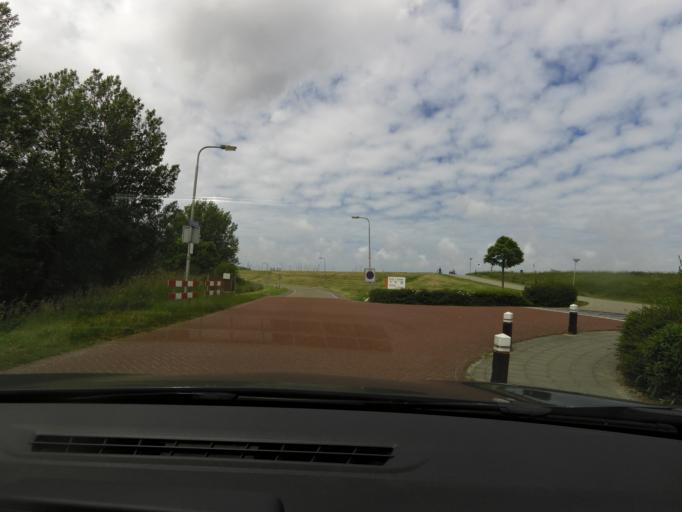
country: NL
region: Zeeland
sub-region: Schouwen-Duiveland
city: Scharendijke
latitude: 51.7391
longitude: 3.8952
